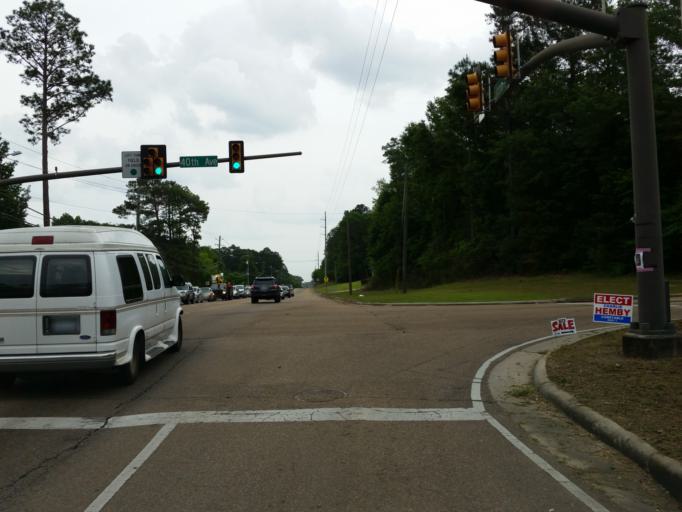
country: US
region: Mississippi
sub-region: Lamar County
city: West Hattiesburg
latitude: 31.3042
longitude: -89.3482
